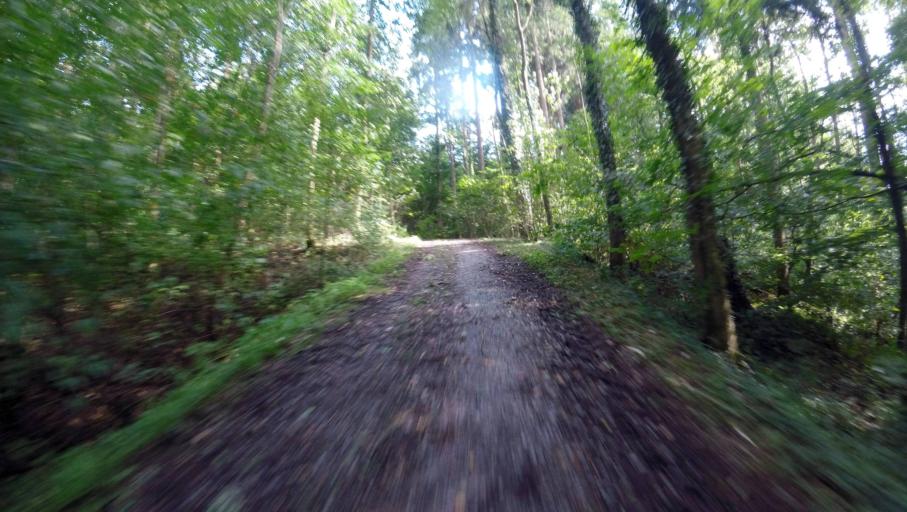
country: DE
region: Baden-Wuerttemberg
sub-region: Regierungsbezirk Stuttgart
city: Aspach
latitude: 48.9777
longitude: 9.4213
